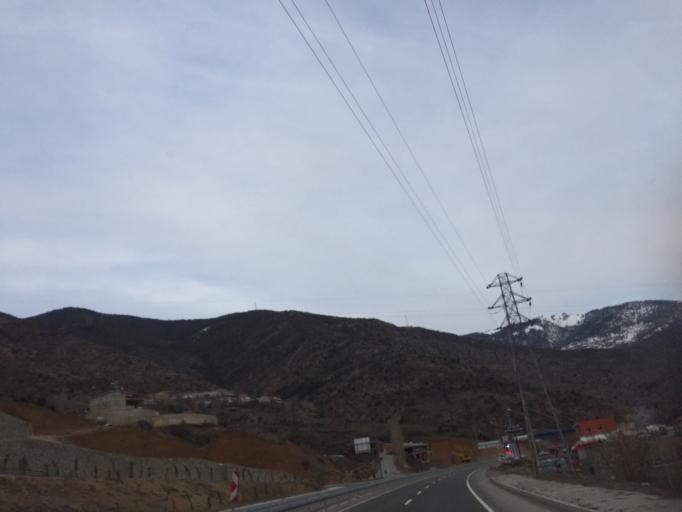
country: TR
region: Gumushane
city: Torul
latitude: 40.5508
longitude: 39.3072
